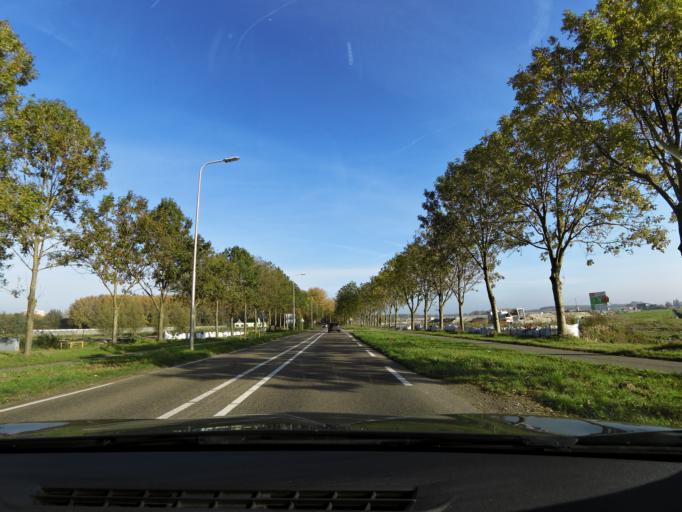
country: NL
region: South Holland
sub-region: Gemeente Ridderkerk
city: Ridderkerk
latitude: 51.8666
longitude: 4.5720
